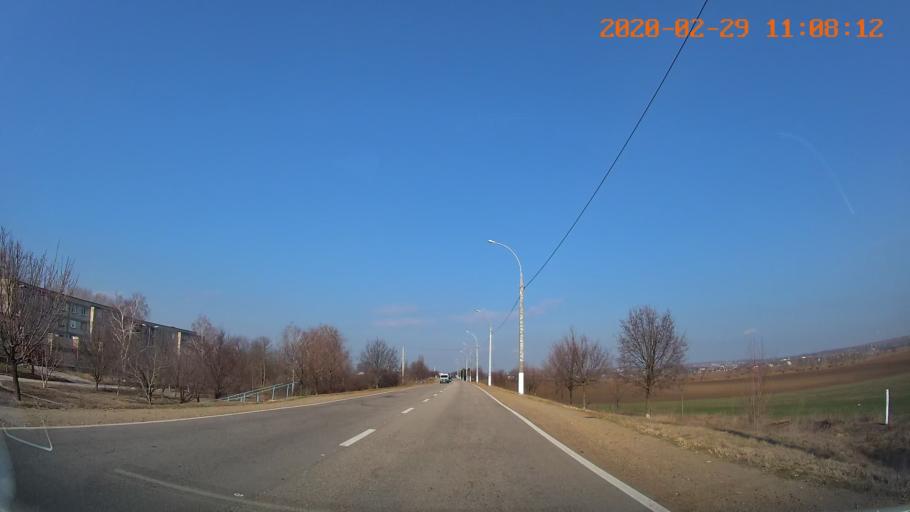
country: MD
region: Criuleni
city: Criuleni
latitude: 47.2319
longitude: 29.1772
